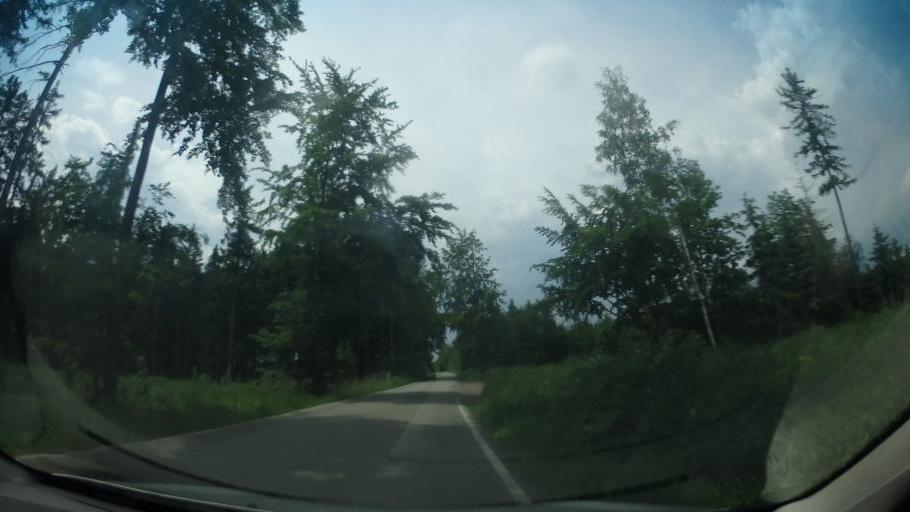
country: CZ
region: South Moravian
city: Lysice
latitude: 49.4573
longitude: 16.4892
